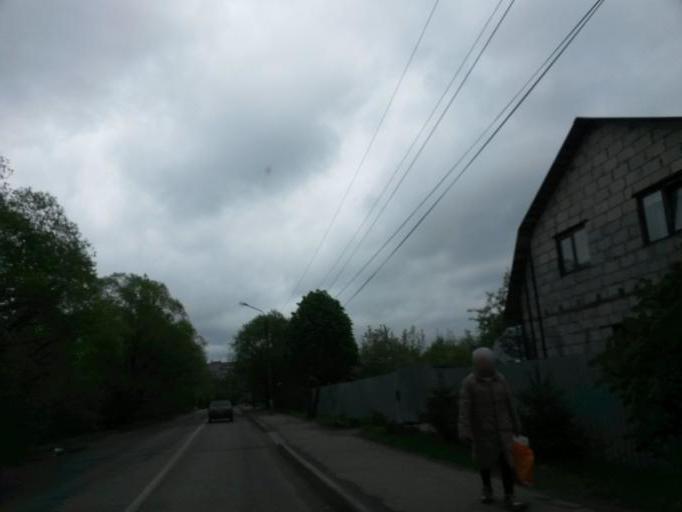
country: RU
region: Moskovskaya
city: Klimovsk
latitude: 55.3593
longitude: 37.5337
